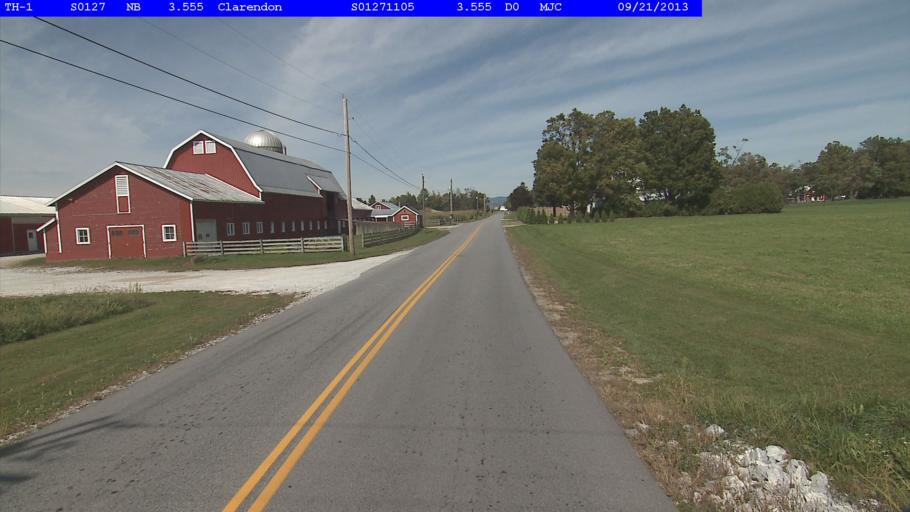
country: US
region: Vermont
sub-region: Rutland County
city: Rutland
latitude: 43.5645
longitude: -72.9727
